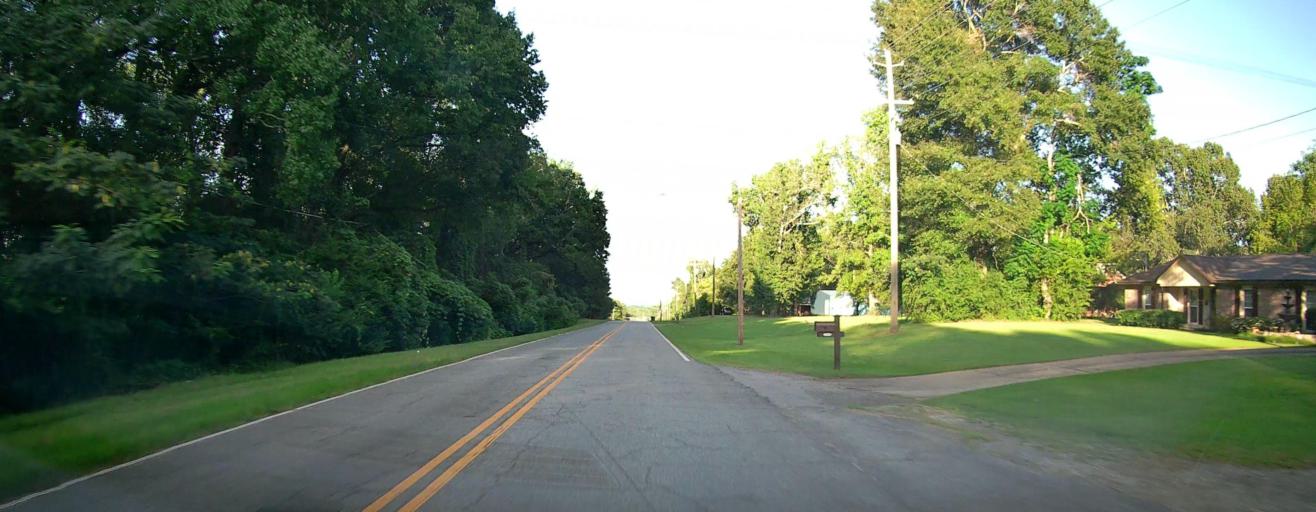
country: US
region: Georgia
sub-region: Muscogee County
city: Columbus
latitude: 32.4230
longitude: -85.0263
